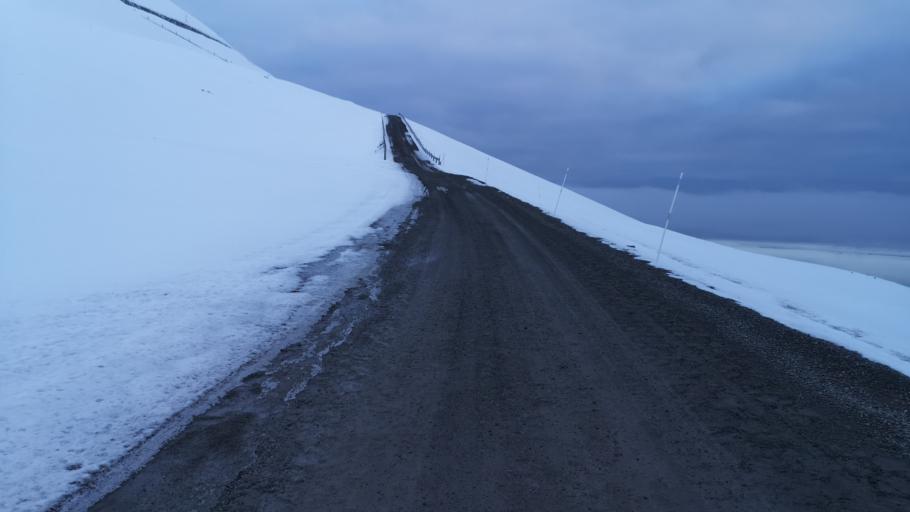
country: SJ
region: Svalbard
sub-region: Spitsbergen
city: Longyearbyen
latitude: 78.2387
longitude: 15.4239
